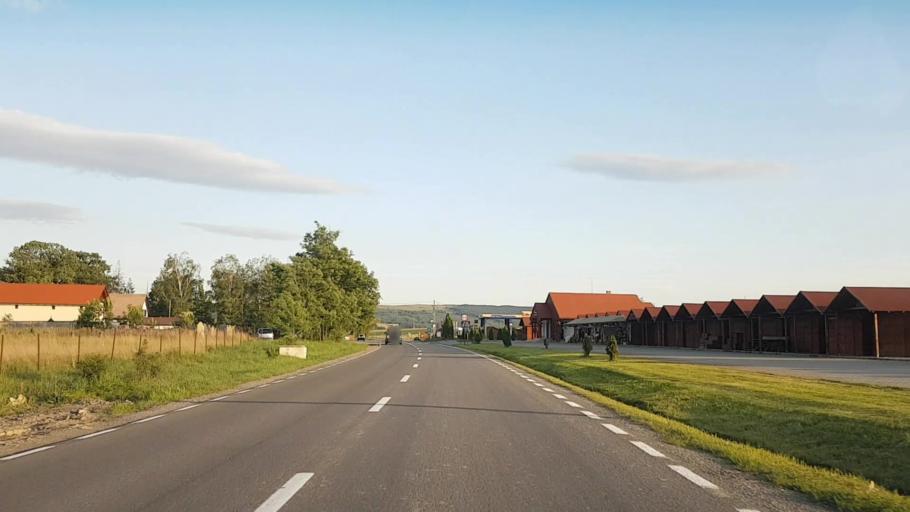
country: RO
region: Harghita
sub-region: Comuna Lupeni
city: Lupeni
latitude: 46.3779
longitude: 25.2194
